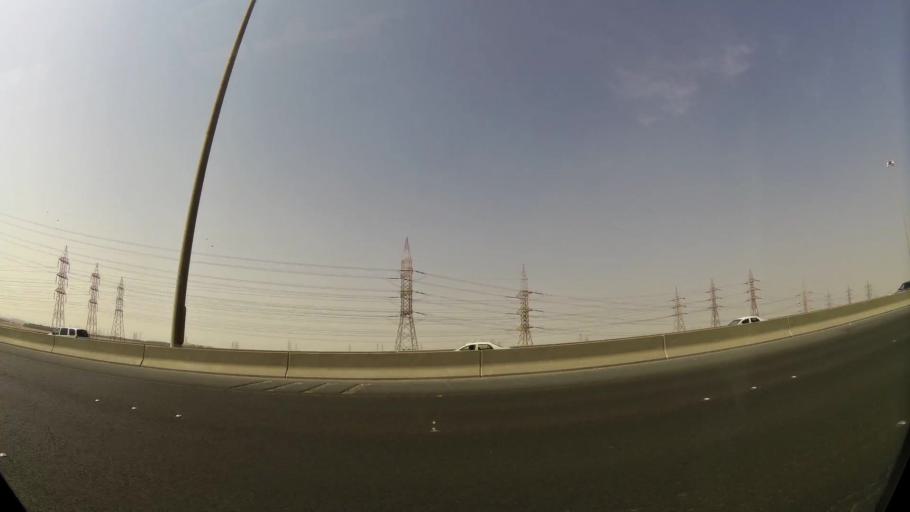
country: KW
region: Al Ahmadi
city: Al Ahmadi
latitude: 29.0594
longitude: 48.1085
